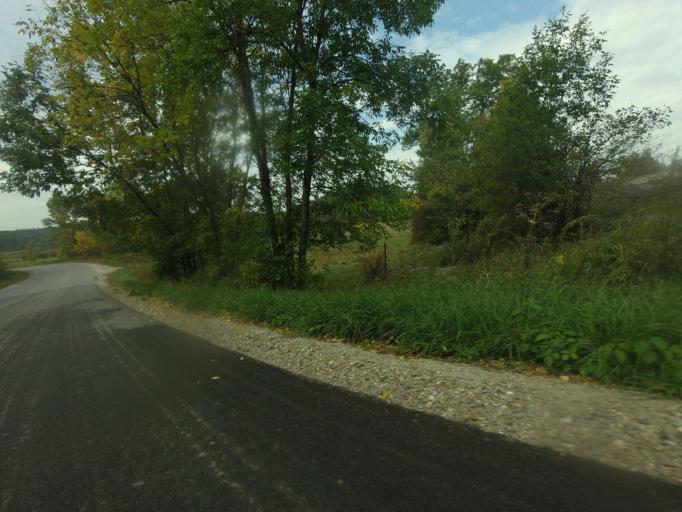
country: CA
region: Quebec
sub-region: Outaouais
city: Wakefield
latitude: 45.9800
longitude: -75.9342
